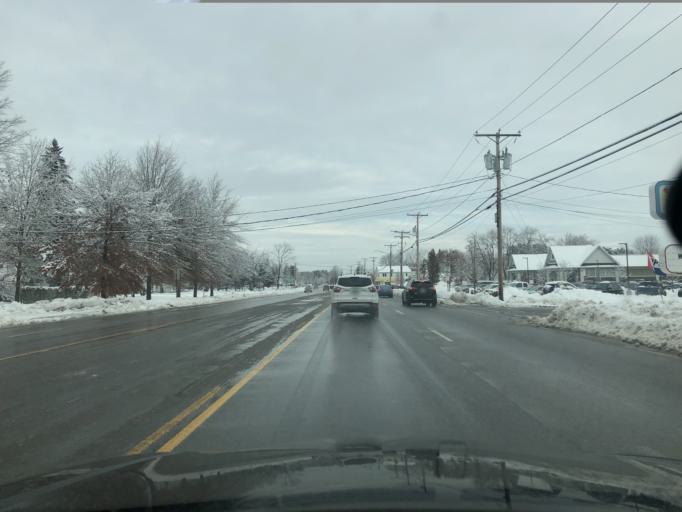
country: US
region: New Hampshire
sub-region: Strafford County
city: Dover
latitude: 43.2294
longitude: -70.8828
